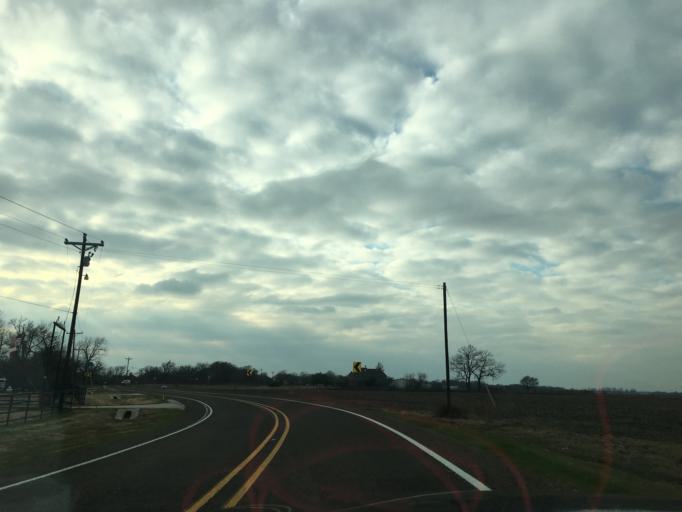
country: US
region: Texas
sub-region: Ellis County
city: Palmer
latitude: 32.4489
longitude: -96.7095
